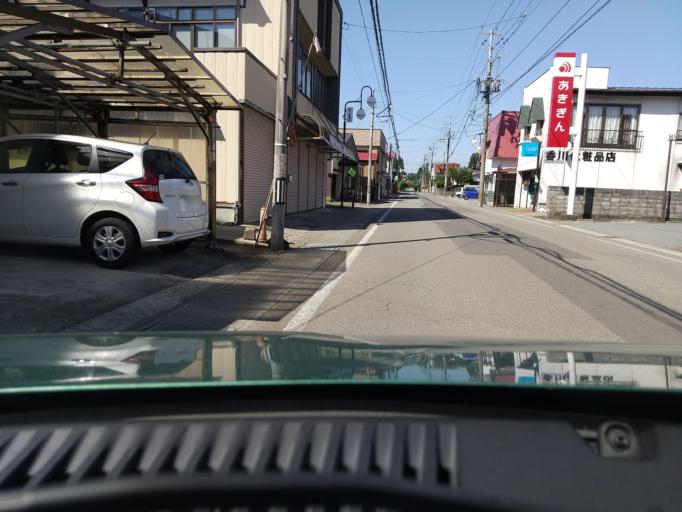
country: JP
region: Akita
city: Akita
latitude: 39.6175
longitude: 140.3207
